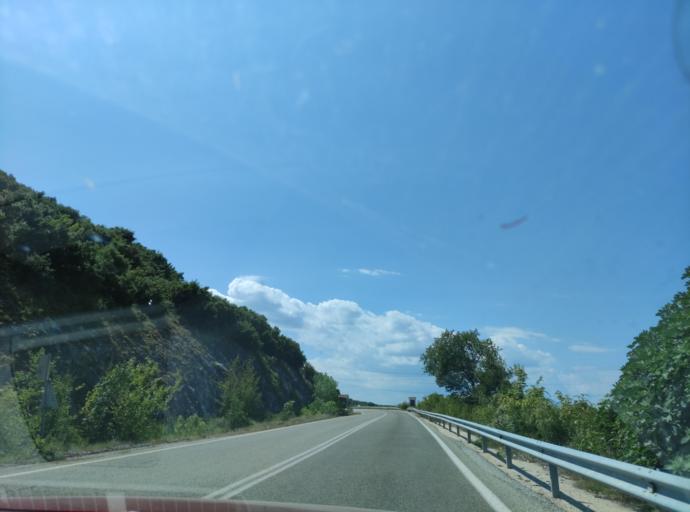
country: GR
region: East Macedonia and Thrace
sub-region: Nomos Kavalas
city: Nikisiani
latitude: 40.9872
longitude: 24.0994
